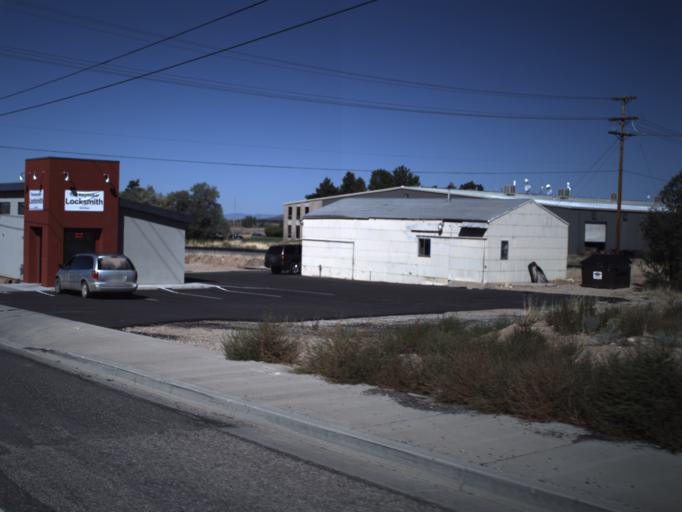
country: US
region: Utah
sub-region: Iron County
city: Cedar City
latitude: 37.6851
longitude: -113.1016
